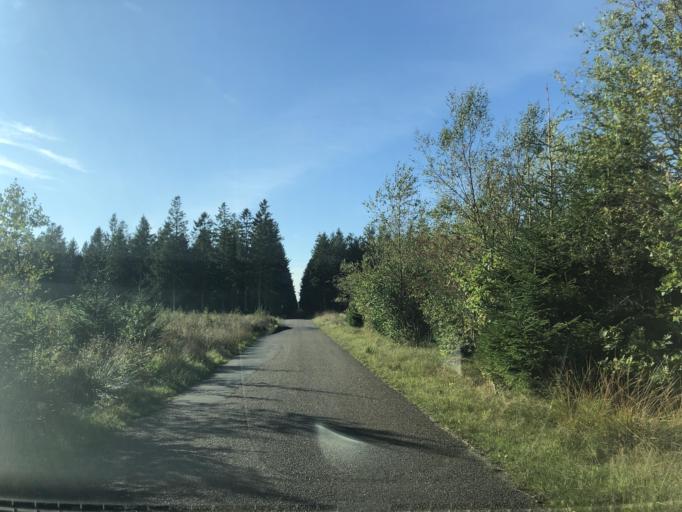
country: DK
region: Central Jutland
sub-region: Holstebro Kommune
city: Holstebro
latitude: 56.3185
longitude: 8.5083
